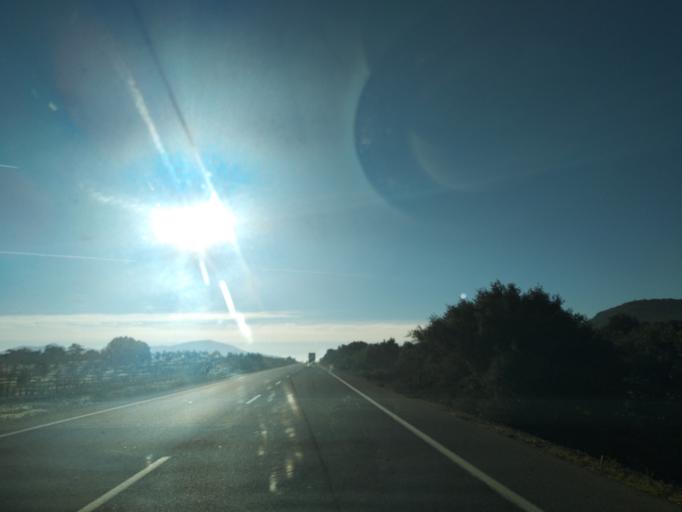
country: ES
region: Andalusia
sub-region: Provincia de Malaga
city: Campillos
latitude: 37.0045
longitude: -4.8446
